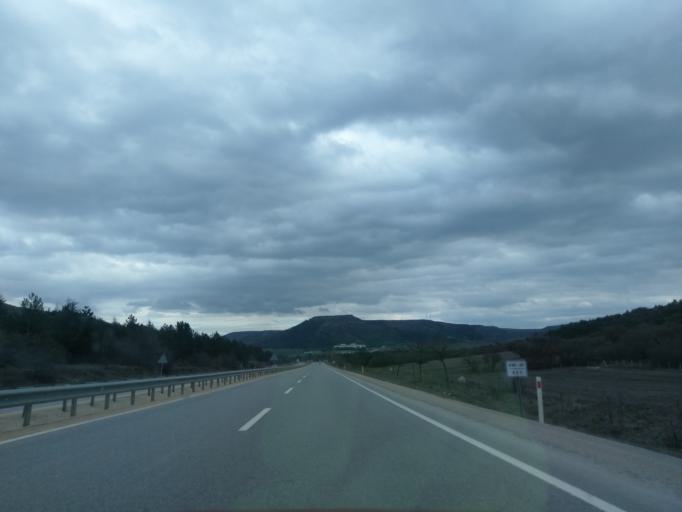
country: TR
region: Eskisehir
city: Eskisehir
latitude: 39.7419
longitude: 30.4148
